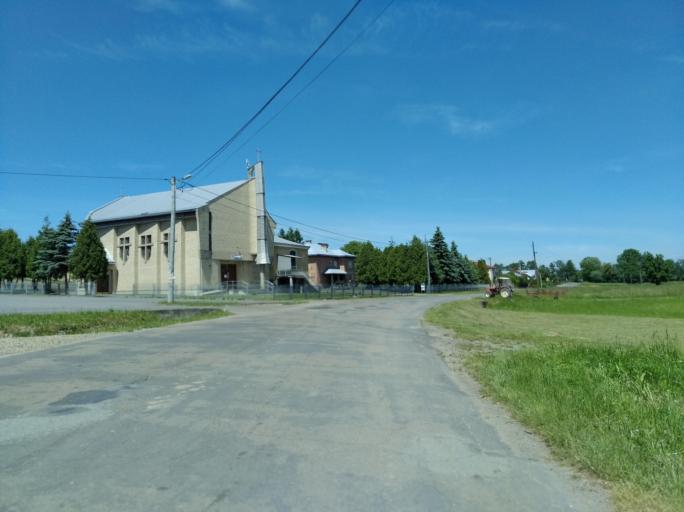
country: PL
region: Subcarpathian Voivodeship
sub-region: Powiat jasielski
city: Tarnowiec
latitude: 49.6995
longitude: 21.5531
